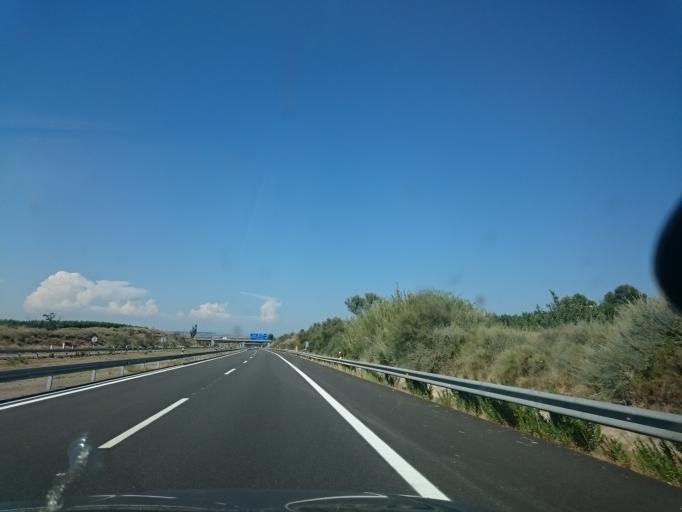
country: ES
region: Catalonia
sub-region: Provincia de Lleida
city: Soses
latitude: 41.5271
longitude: 0.4691
